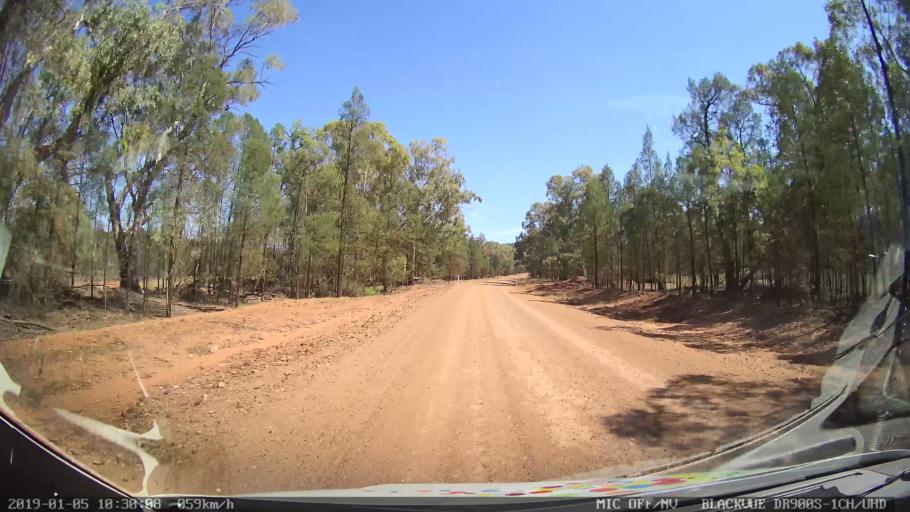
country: AU
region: New South Wales
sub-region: Gilgandra
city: Gilgandra
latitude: -31.5351
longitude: 148.9253
